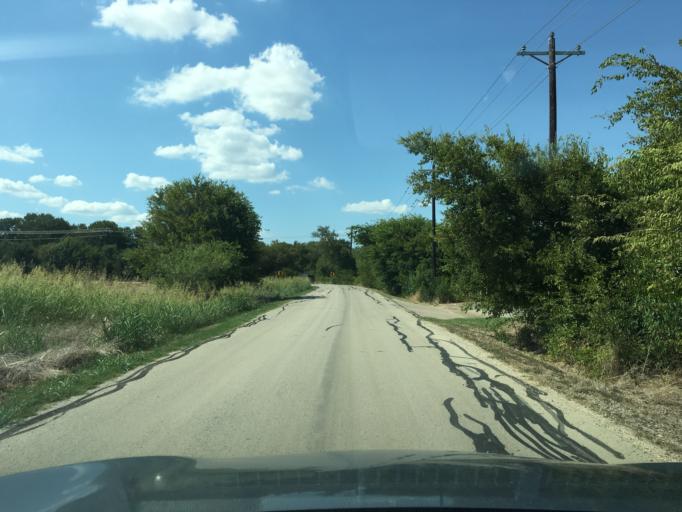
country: US
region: Texas
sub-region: Tarrant County
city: Mansfield
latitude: 32.5253
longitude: -97.0788
